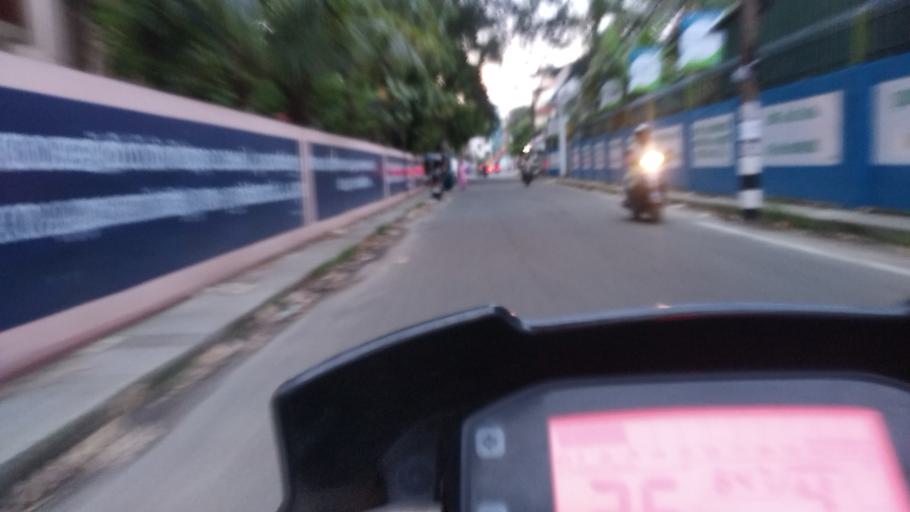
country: IN
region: Kerala
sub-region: Ernakulam
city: Elur
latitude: 10.0063
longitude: 76.2766
